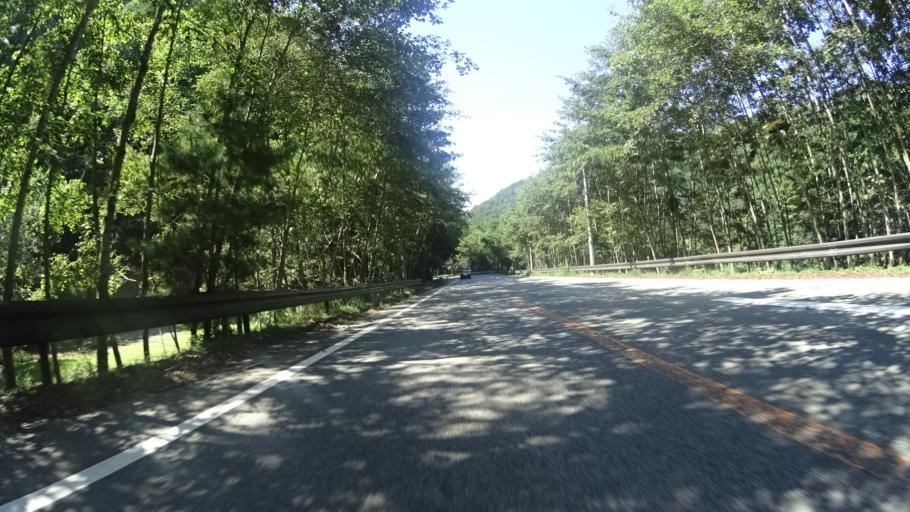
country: JP
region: Yamanashi
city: Enzan
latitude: 35.7577
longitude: 138.8086
